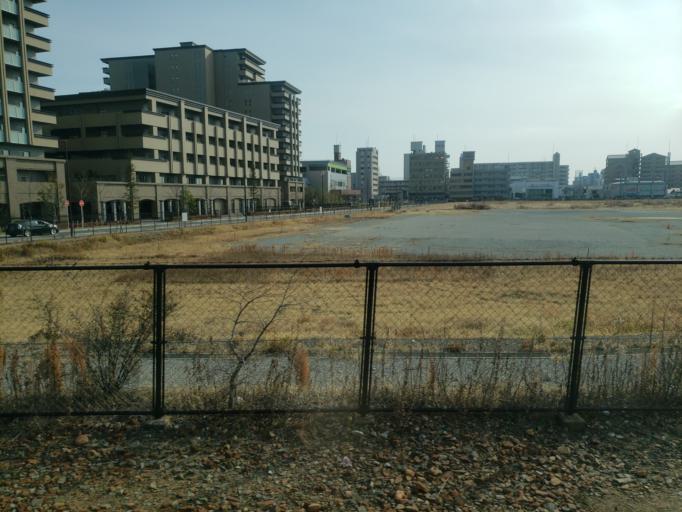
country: JP
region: Hyogo
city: Nishinomiya-hama
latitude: 34.7388
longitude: 135.3568
